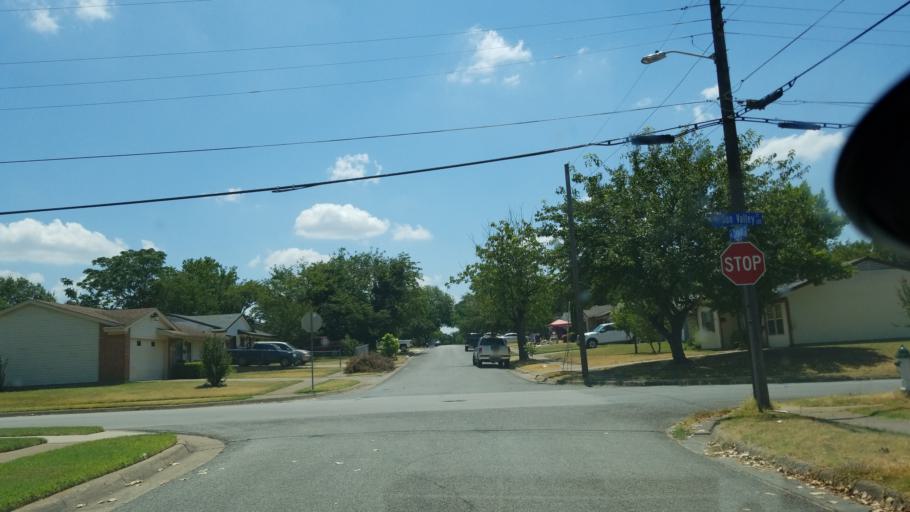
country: US
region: Texas
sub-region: Dallas County
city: Duncanville
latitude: 32.6682
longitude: -96.8951
